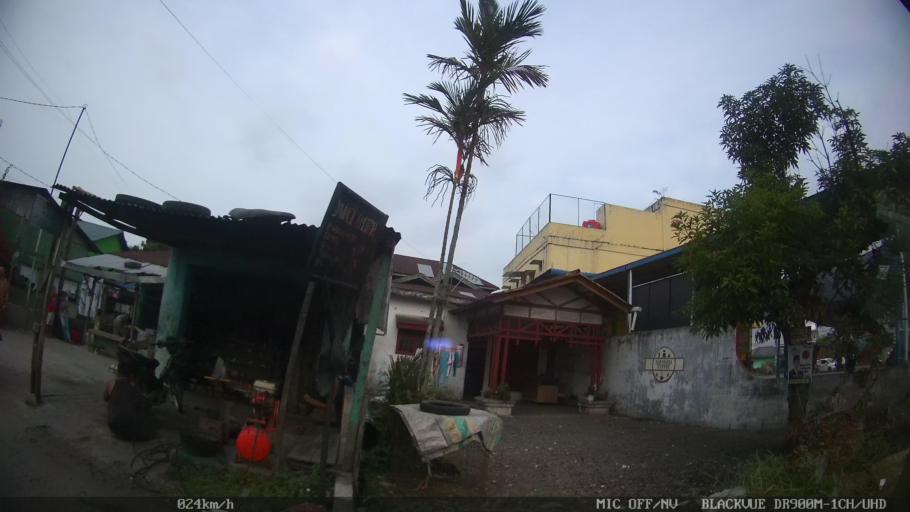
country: ID
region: North Sumatra
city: Sunggal
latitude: 3.5853
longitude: 98.5994
